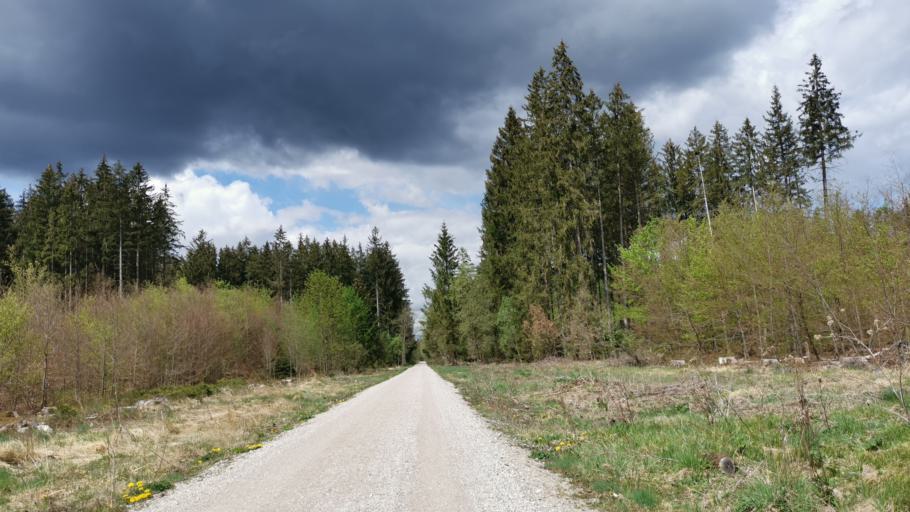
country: DE
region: Bavaria
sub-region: Upper Bavaria
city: Neuried
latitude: 48.0611
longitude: 11.4466
